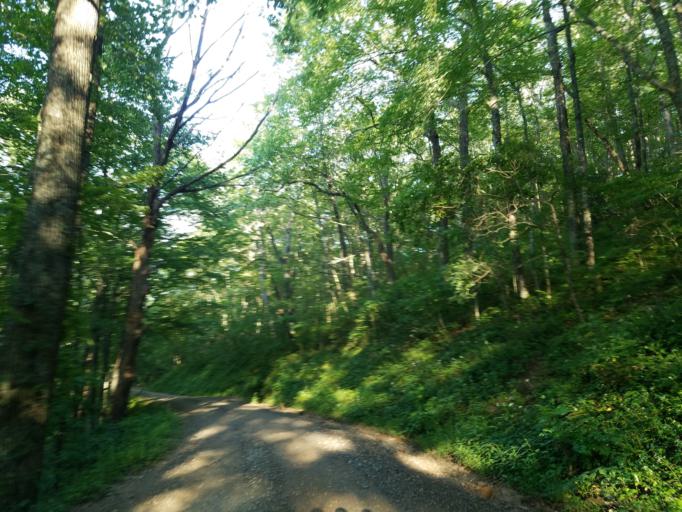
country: US
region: Georgia
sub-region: Lumpkin County
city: Dahlonega
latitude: 34.6577
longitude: -84.1088
